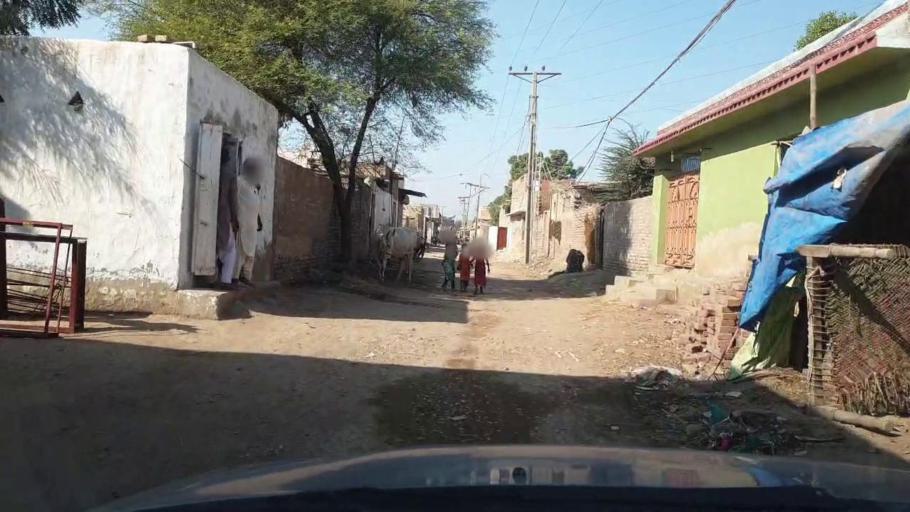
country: PK
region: Sindh
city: Tando Muhammad Khan
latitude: 25.1319
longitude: 68.5484
